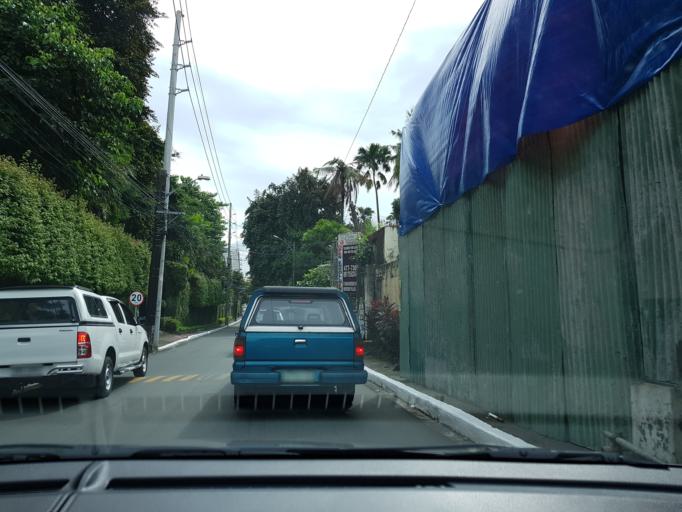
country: PH
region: Metro Manila
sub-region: San Juan
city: San Juan
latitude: 14.6121
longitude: 121.0395
